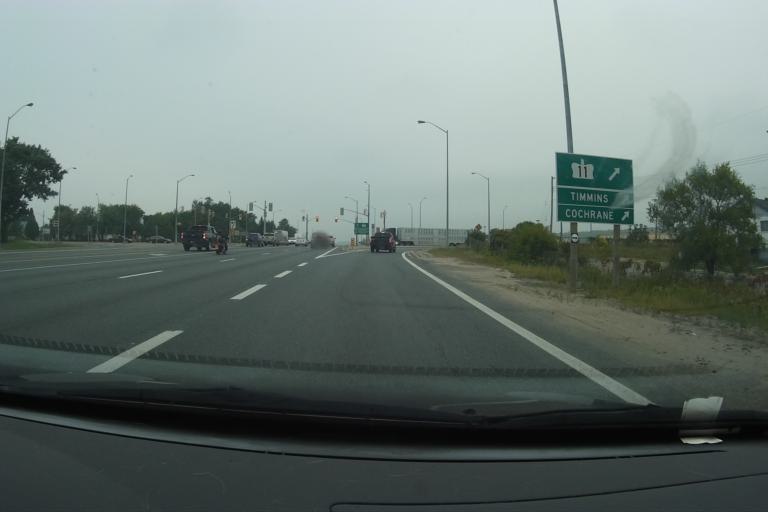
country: CA
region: Ontario
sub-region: Nipissing District
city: North Bay
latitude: 46.3292
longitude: -79.4648
